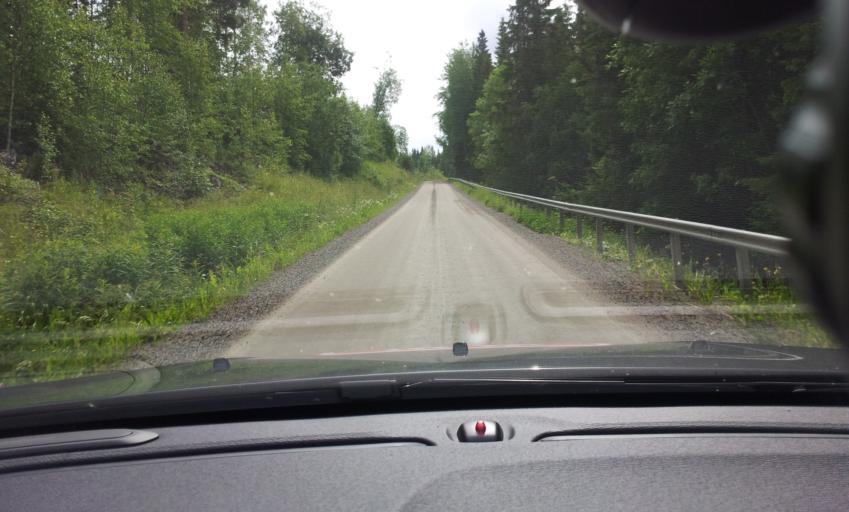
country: SE
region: Jaemtland
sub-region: OEstersunds Kommun
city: Brunflo
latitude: 62.9431
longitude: 14.9542
